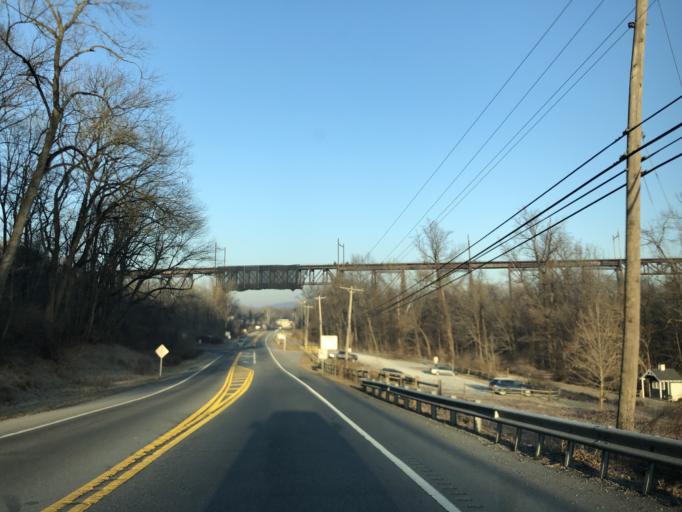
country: US
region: Pennsylvania
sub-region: Chester County
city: Downingtown
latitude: 39.9932
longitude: -75.6966
